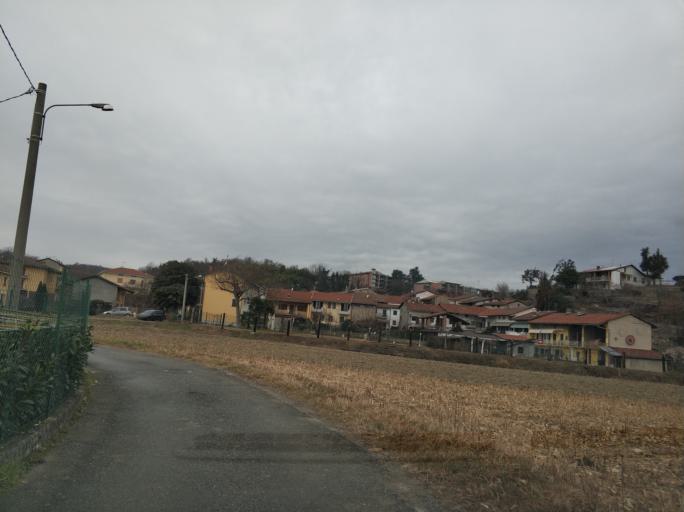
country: IT
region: Piedmont
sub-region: Provincia di Torino
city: Ivrea
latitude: 45.4448
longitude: 7.8809
